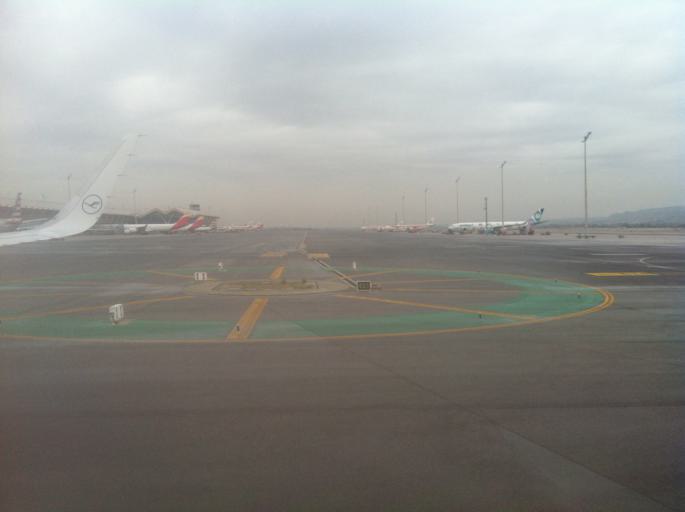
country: ES
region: Madrid
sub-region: Provincia de Madrid
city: Barajas de Madrid
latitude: 40.4879
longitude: -3.5647
